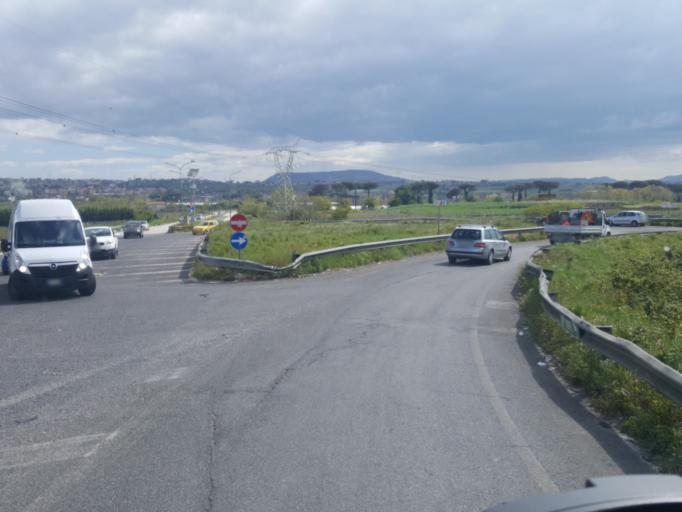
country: IT
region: Campania
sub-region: Provincia di Napoli
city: Torretta-Scalzapecora
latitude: 40.9296
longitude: 14.1224
